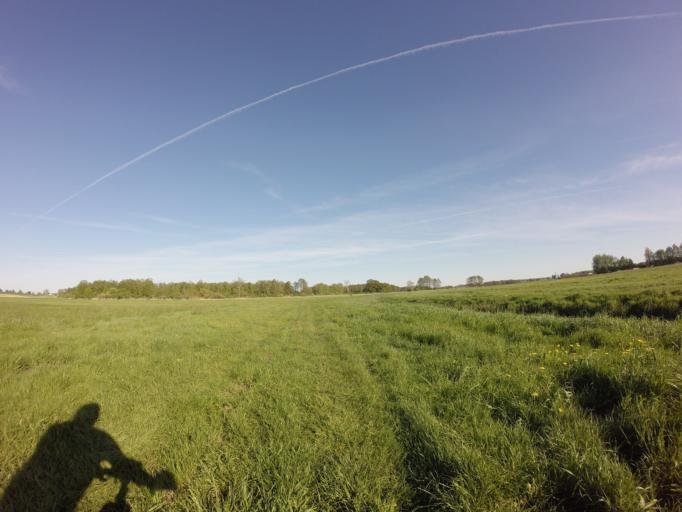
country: PL
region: West Pomeranian Voivodeship
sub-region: Powiat choszczenski
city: Pelczyce
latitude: 53.1292
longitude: 15.3266
